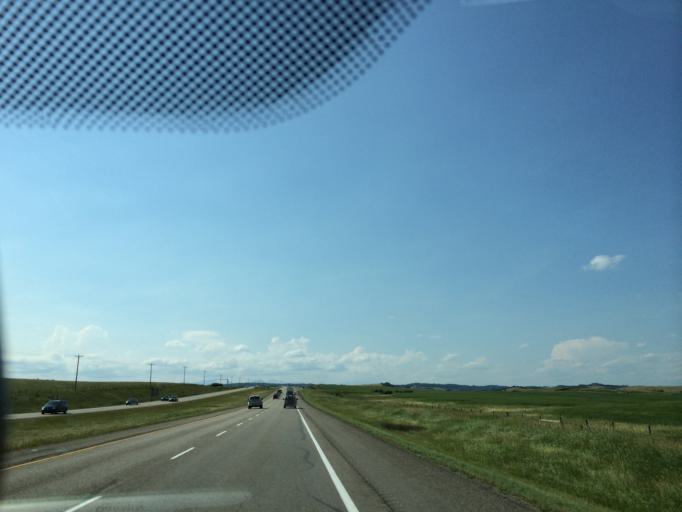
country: CA
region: Alberta
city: Cochrane
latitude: 51.1099
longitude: -114.6382
